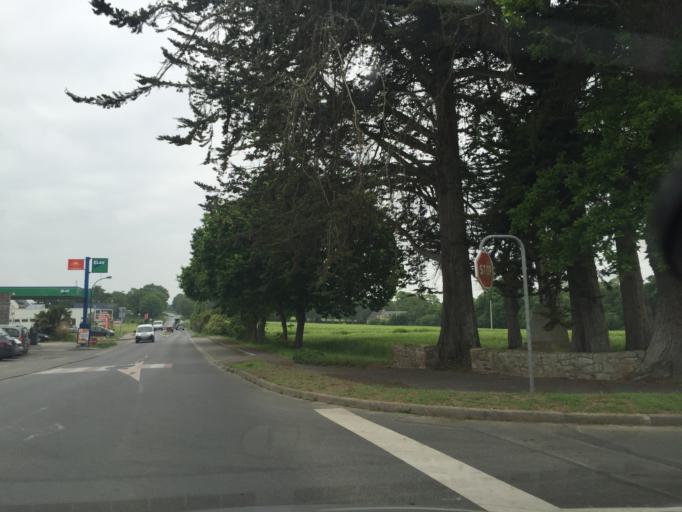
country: FR
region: Brittany
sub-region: Departement des Cotes-d'Armor
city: Henanbihen
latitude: 48.5590
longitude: -2.3794
